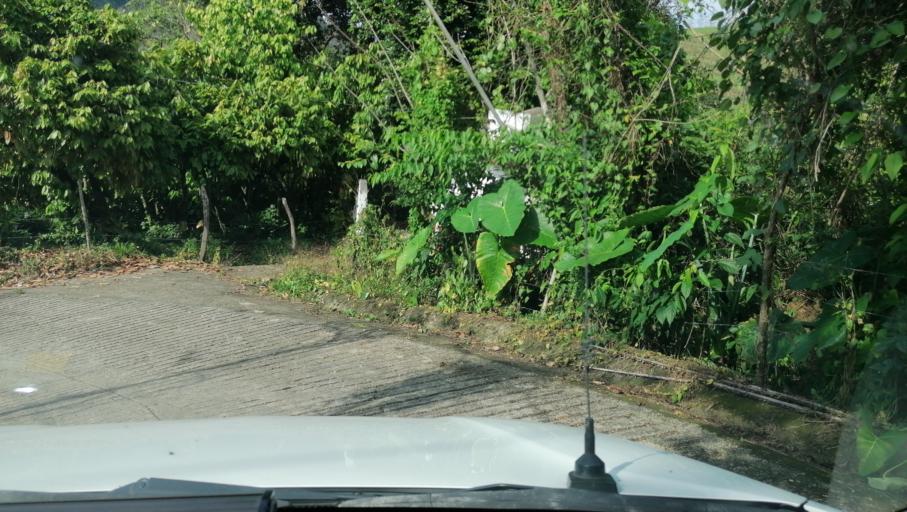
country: MX
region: Chiapas
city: Ostuacan
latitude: 17.4576
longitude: -93.2408
